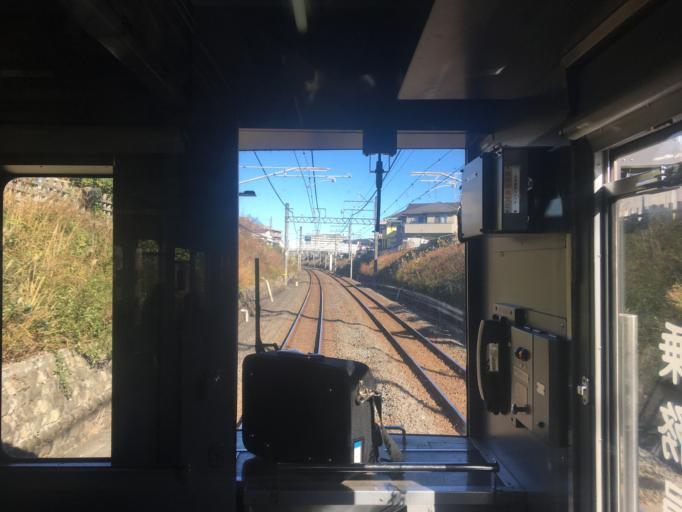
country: JP
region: Saitama
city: Sakado
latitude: 36.0287
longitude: 139.4026
